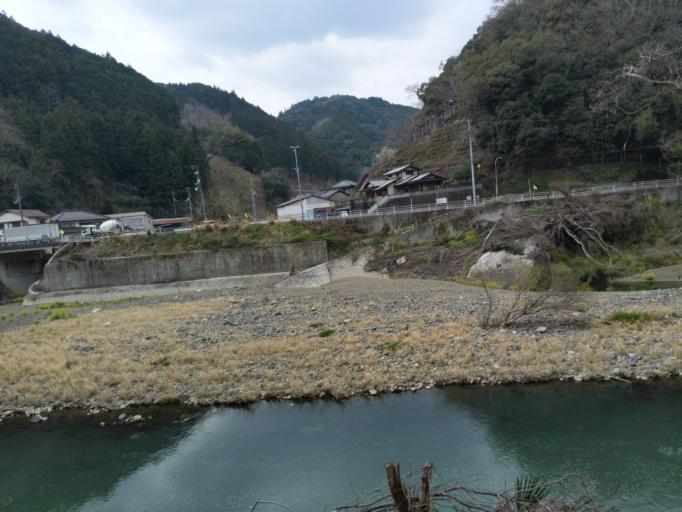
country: JP
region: Ehime
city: Ozu
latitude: 33.4564
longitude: 132.6801
